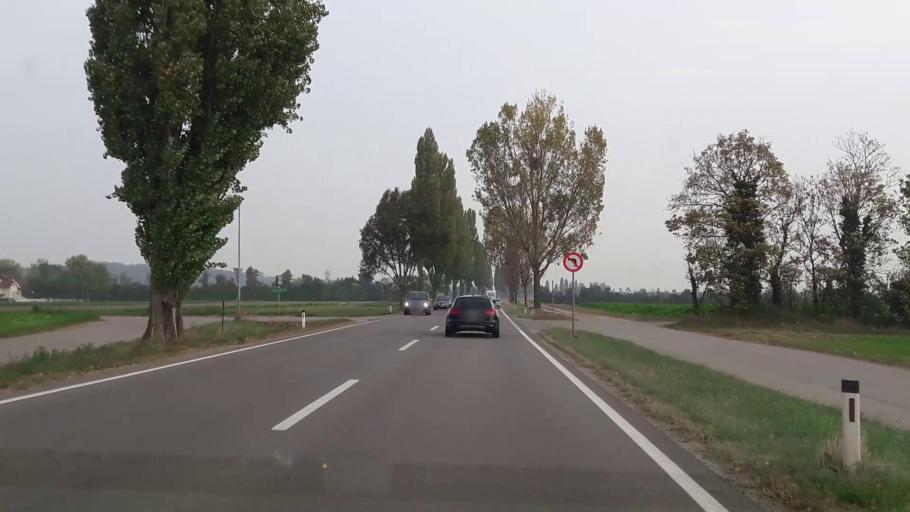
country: AT
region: Lower Austria
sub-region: Politischer Bezirk Bruck an der Leitha
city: Trautmannsdorf an der Leitha
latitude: 48.0510
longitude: 16.6438
